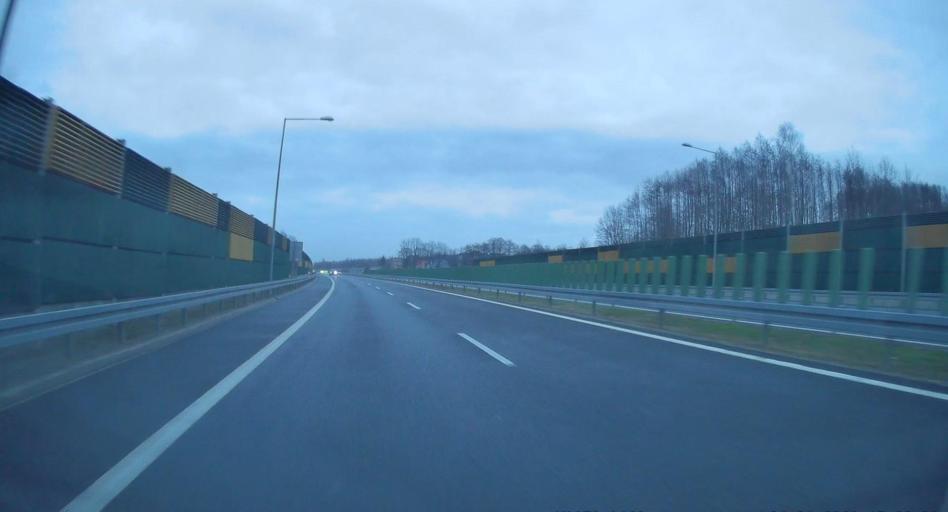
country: PL
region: Subcarpathian Voivodeship
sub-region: Powiat ropczycko-sedziszowski
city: Ropczyce
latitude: 50.0492
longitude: 21.6098
